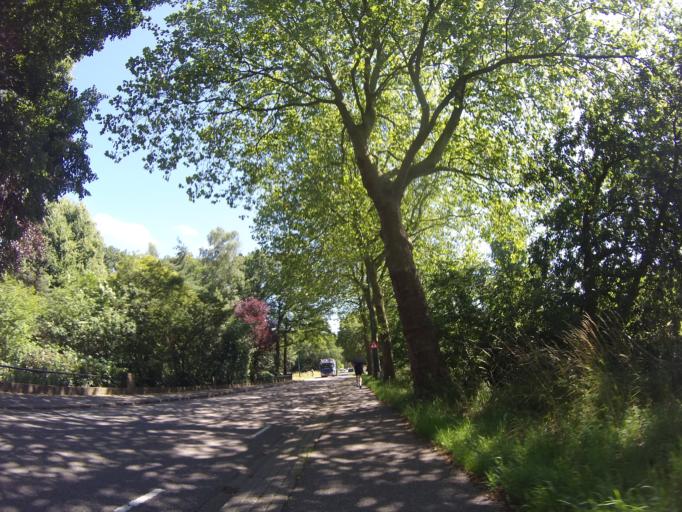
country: NL
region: Utrecht
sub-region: Gemeente De Bilt
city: De Bilt
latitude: 52.1174
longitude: 5.1717
